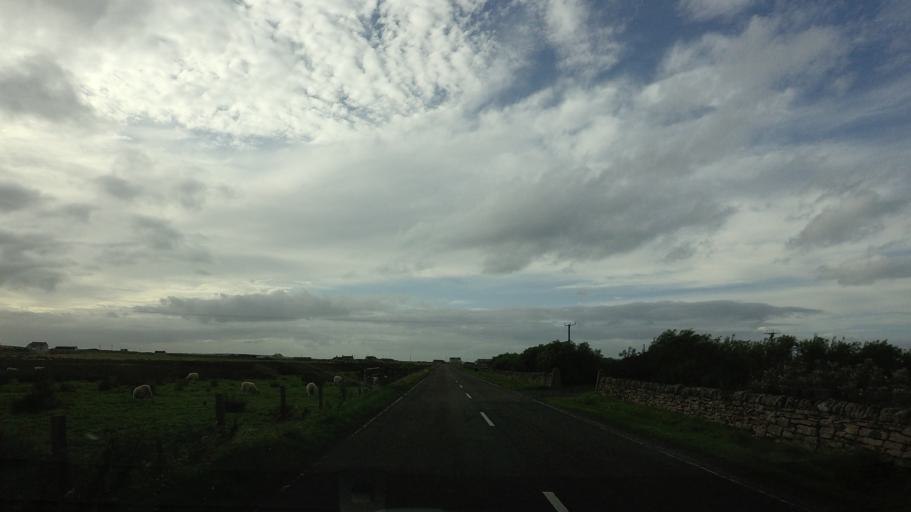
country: GB
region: Scotland
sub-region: Highland
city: Wick
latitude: 58.6409
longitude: -3.0768
